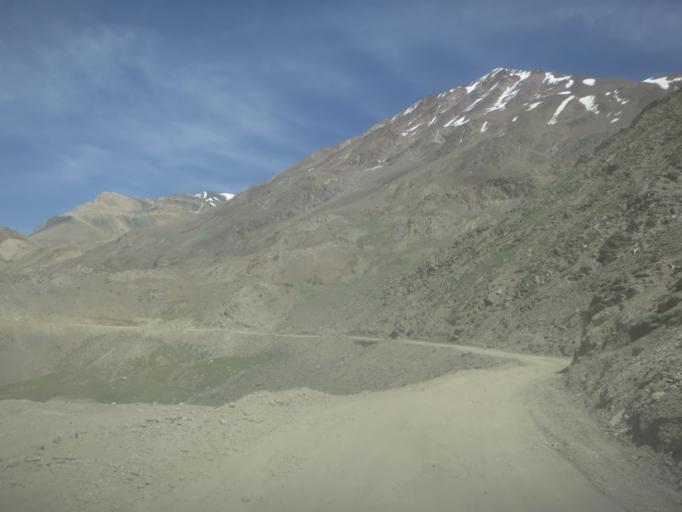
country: IN
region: Himachal Pradesh
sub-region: Kulu
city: Manali
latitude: 32.4228
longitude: 77.6537
